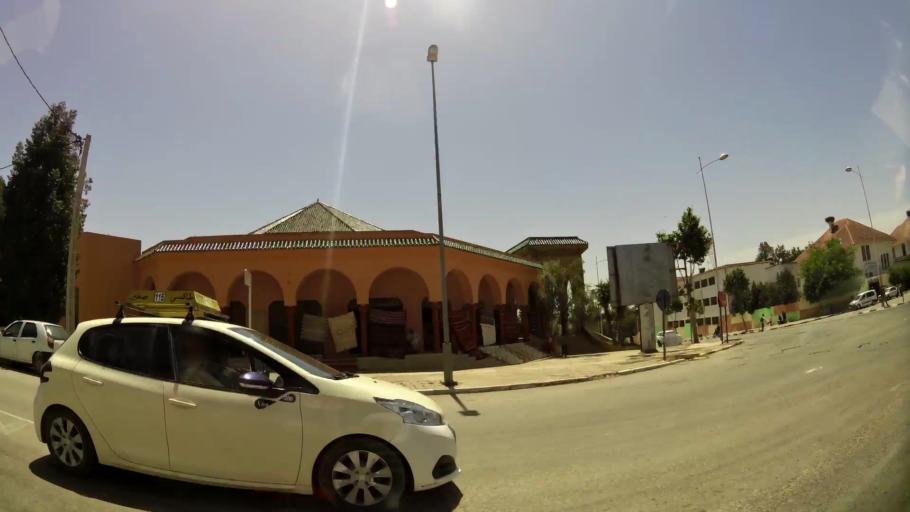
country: MA
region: Rabat-Sale-Zemmour-Zaer
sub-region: Khemisset
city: Khemisset
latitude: 33.8242
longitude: -6.0632
